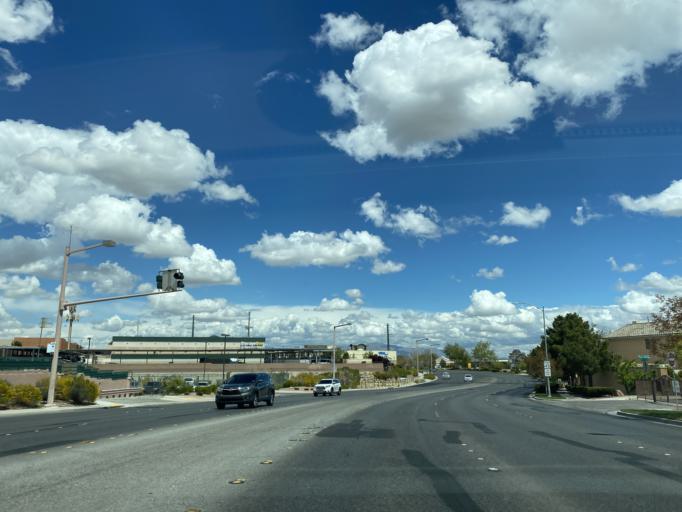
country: US
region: Nevada
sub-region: Clark County
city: Summerlin South
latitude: 36.1558
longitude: -115.3155
